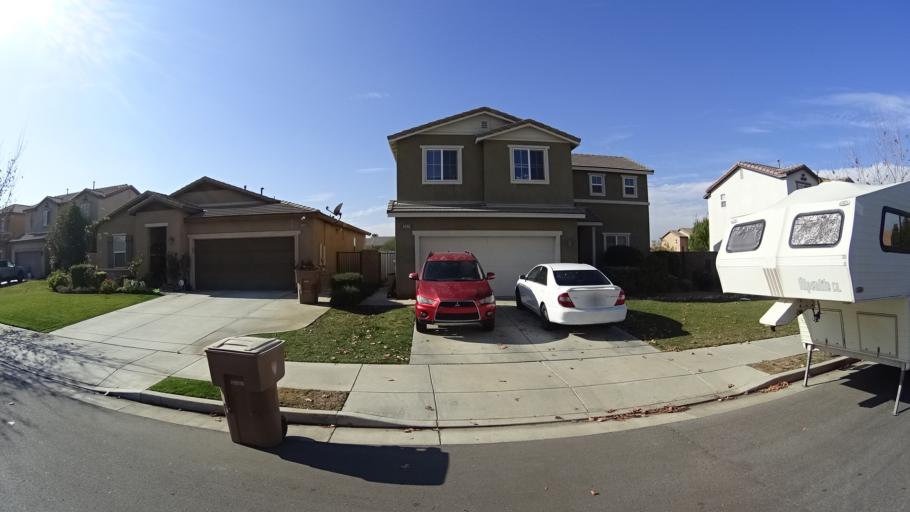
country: US
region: California
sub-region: Kern County
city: Oildale
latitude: 35.4054
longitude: -118.8906
